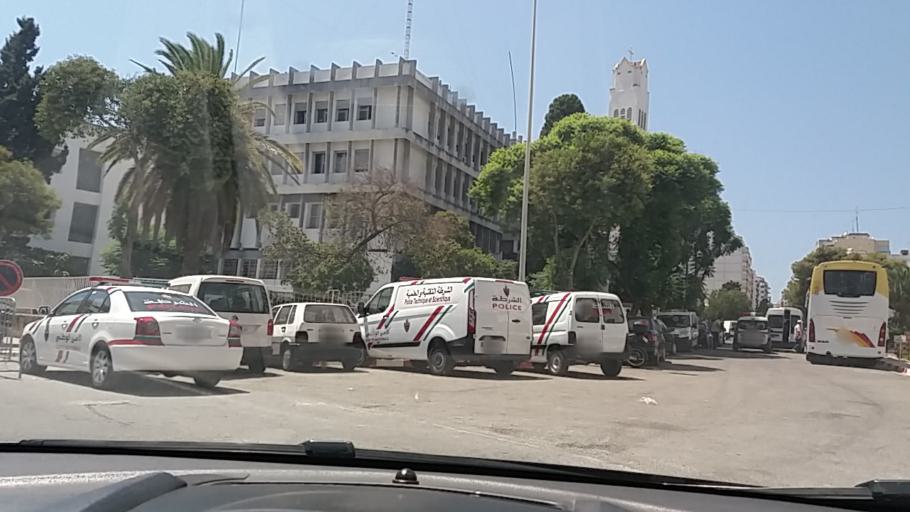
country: MA
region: Tanger-Tetouan
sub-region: Tanger-Assilah
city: Tangier
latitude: 35.7751
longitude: -5.8058
